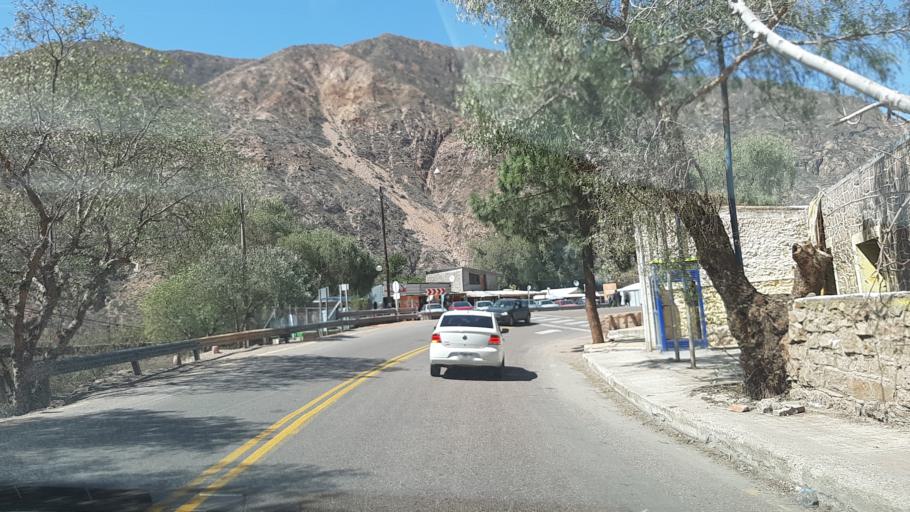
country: AR
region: Mendoza
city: Lujan de Cuyo
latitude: -33.0128
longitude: -69.1196
